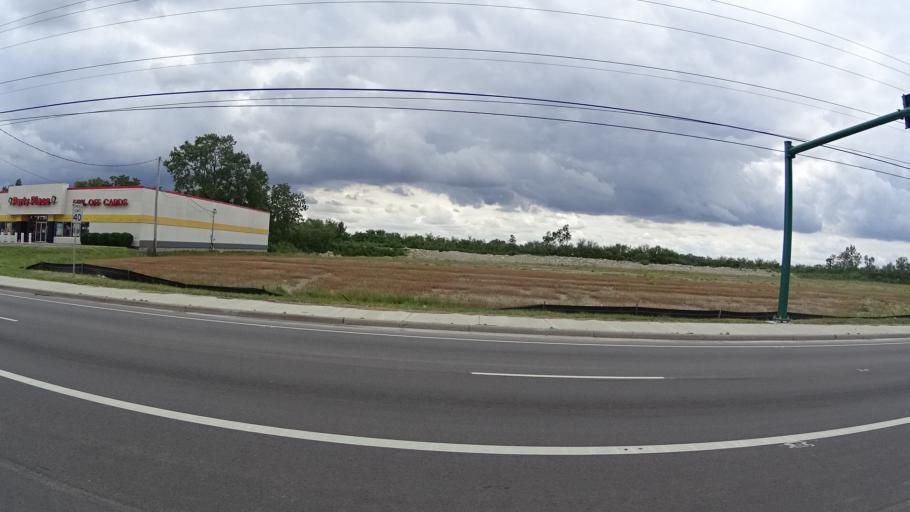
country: US
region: Ohio
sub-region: Erie County
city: Sandusky
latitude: 41.4097
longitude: -82.6655
